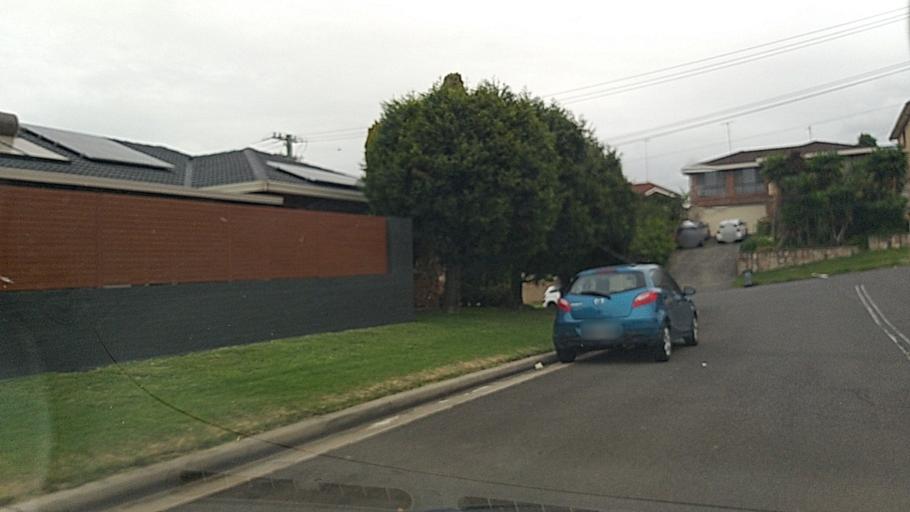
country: AU
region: New South Wales
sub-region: Wollongong
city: Lake Heights
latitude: -34.4851
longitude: 150.8791
